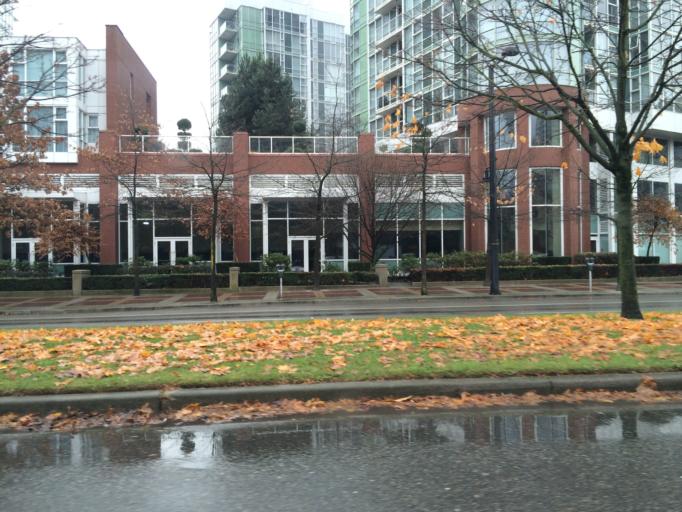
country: CA
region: British Columbia
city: West End
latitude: 49.2745
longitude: -123.1182
